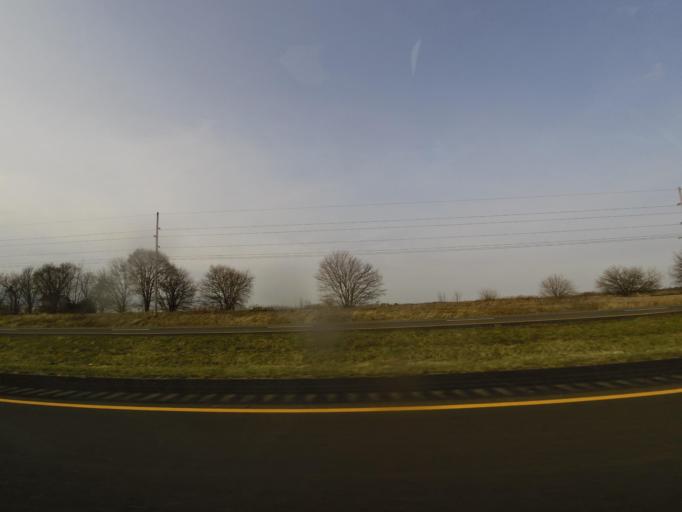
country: US
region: Illinois
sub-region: Christian County
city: Assumption
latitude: 39.5481
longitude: -89.0410
